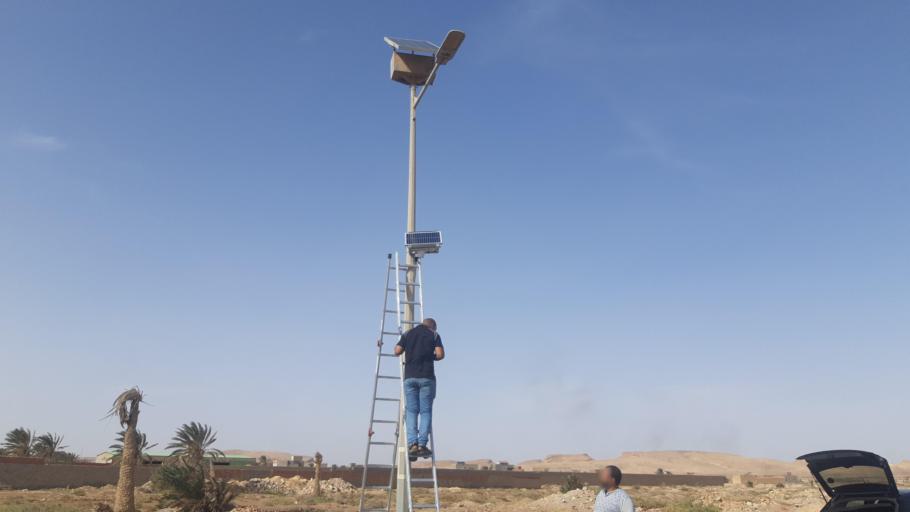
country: TN
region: Qibili
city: Kebili
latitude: 33.7275
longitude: 8.9480
